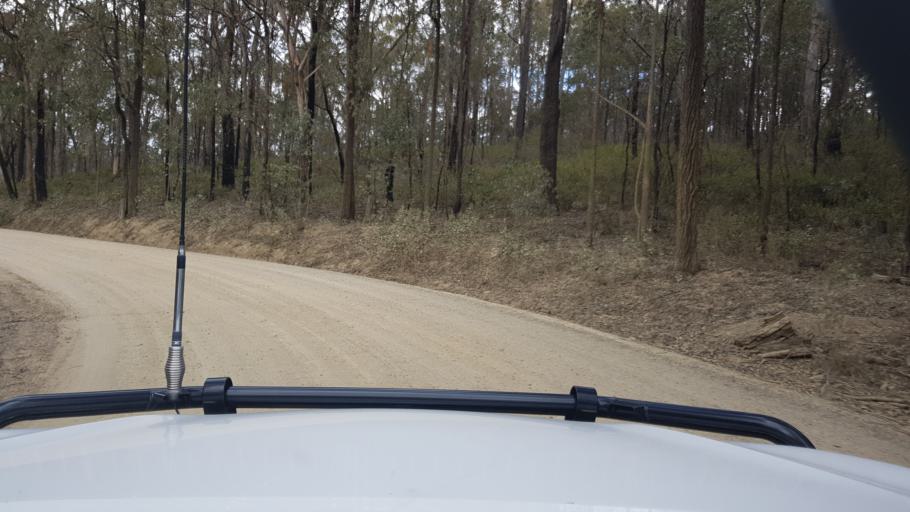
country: AU
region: Victoria
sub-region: East Gippsland
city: Bairnsdale
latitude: -37.6982
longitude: 147.5744
